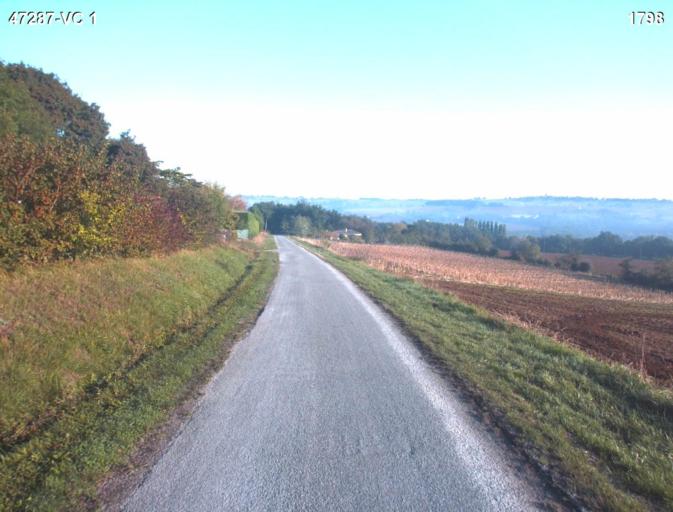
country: FR
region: Aquitaine
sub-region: Departement du Lot-et-Garonne
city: Sainte-Colombe-en-Bruilhois
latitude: 44.1369
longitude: 0.4472
